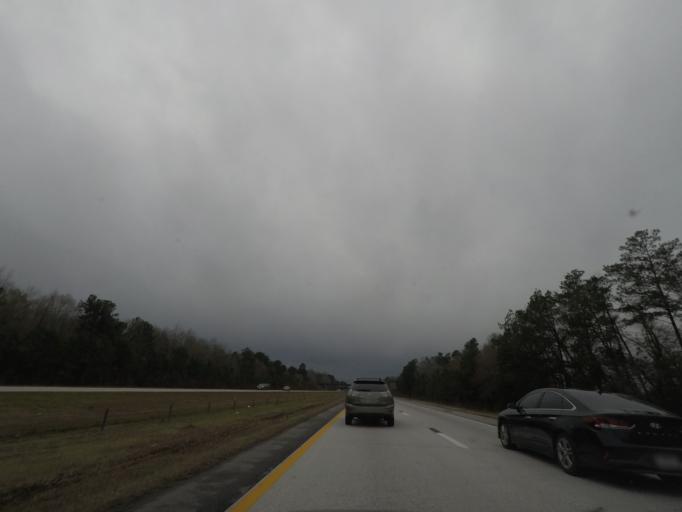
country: US
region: South Carolina
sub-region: Dorchester County
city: Saint George
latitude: 33.2323
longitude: -80.5881
